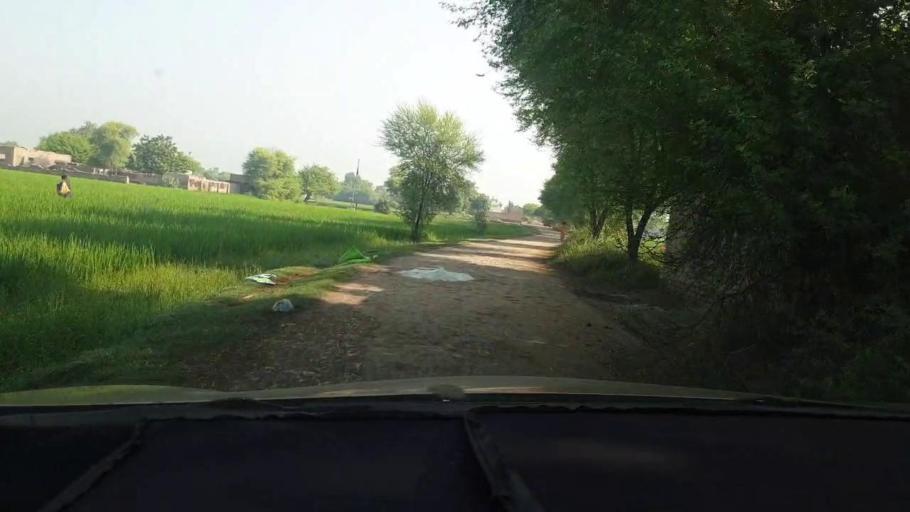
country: PK
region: Sindh
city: Kambar
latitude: 27.5997
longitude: 68.1111
